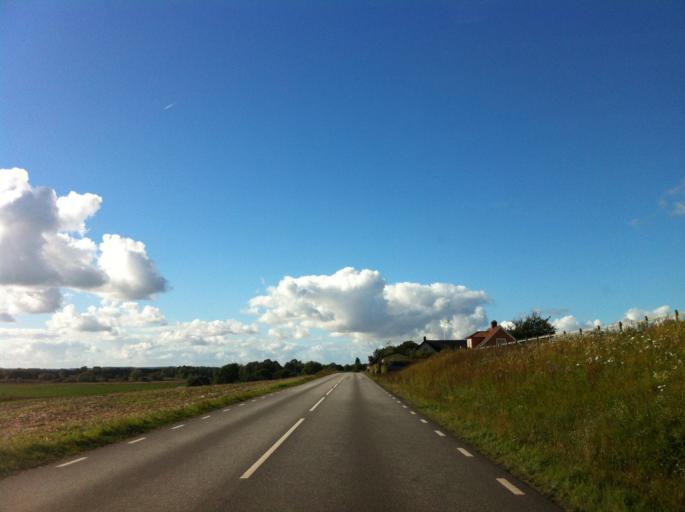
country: SE
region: Skane
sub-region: Hoors Kommun
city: Loberod
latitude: 55.7272
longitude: 13.4900
